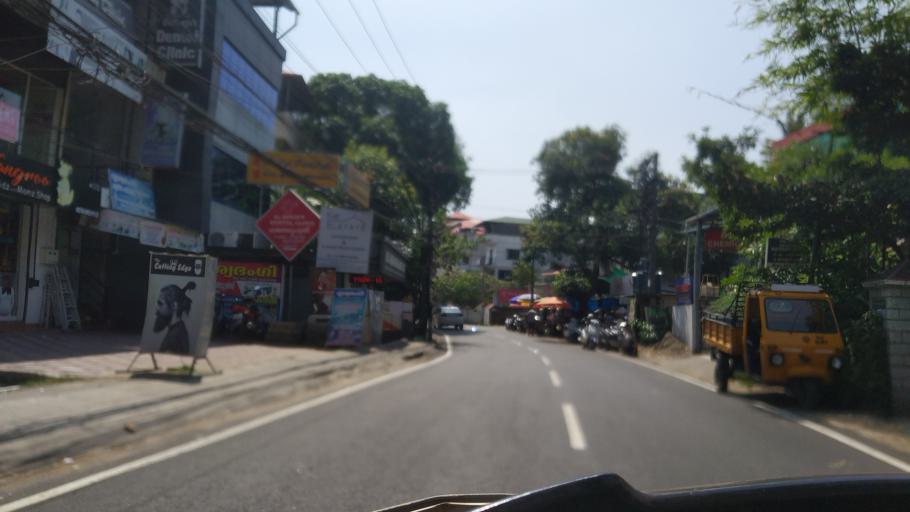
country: IN
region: Kerala
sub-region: Ernakulam
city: Cochin
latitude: 9.9964
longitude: 76.3079
